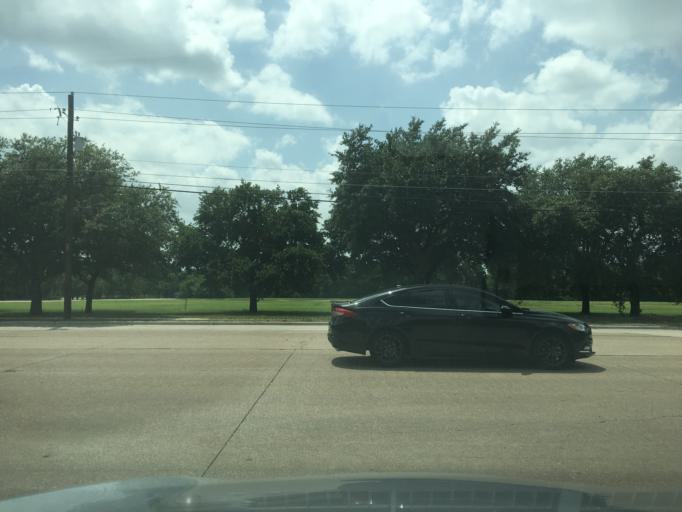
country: US
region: Texas
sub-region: Dallas County
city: Addison
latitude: 32.9082
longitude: -96.8164
